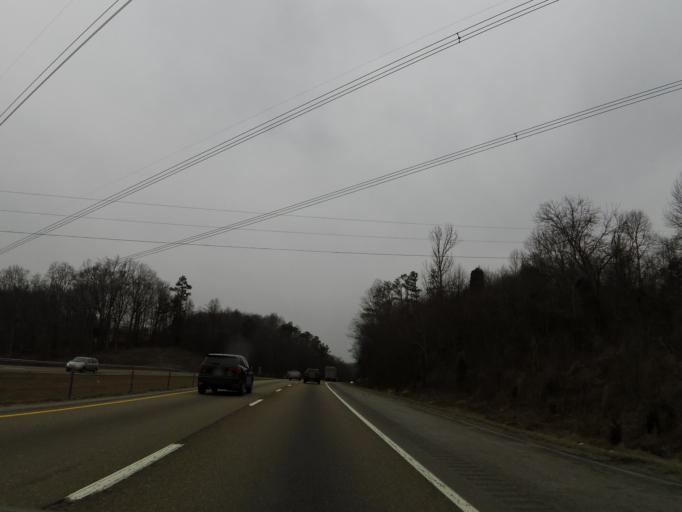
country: US
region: Tennessee
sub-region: Roane County
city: Kingston
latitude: 35.8659
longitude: -84.4301
